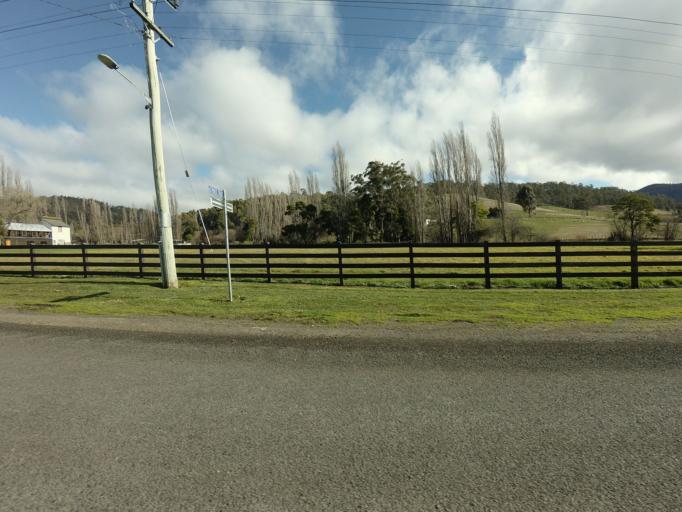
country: AU
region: Tasmania
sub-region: Derwent Valley
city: New Norfolk
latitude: -42.6162
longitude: 146.7156
